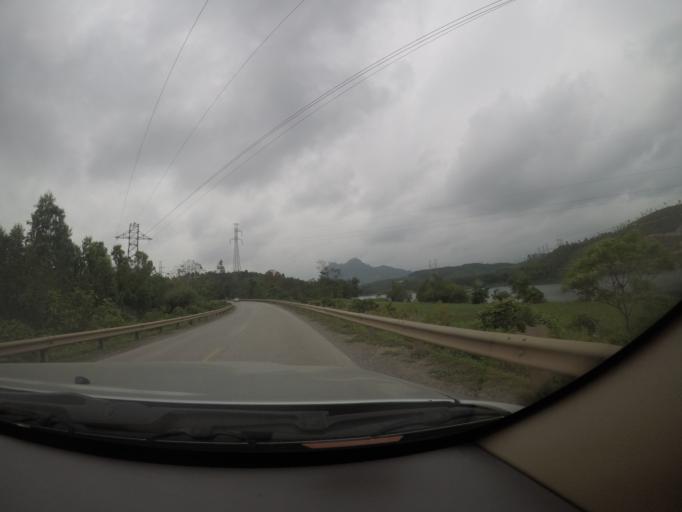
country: VN
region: Quang Binh
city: Quan Hau
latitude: 17.3226
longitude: 106.6235
